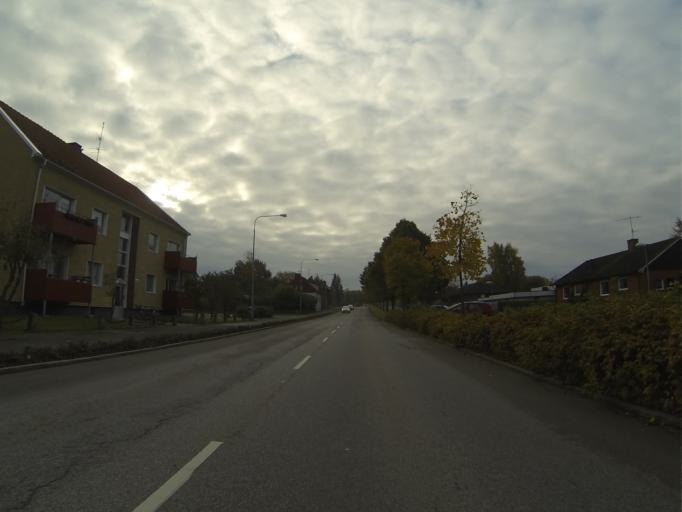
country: SE
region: Skane
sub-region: Tomelilla Kommun
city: Tomelilla
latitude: 55.5432
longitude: 13.9433
